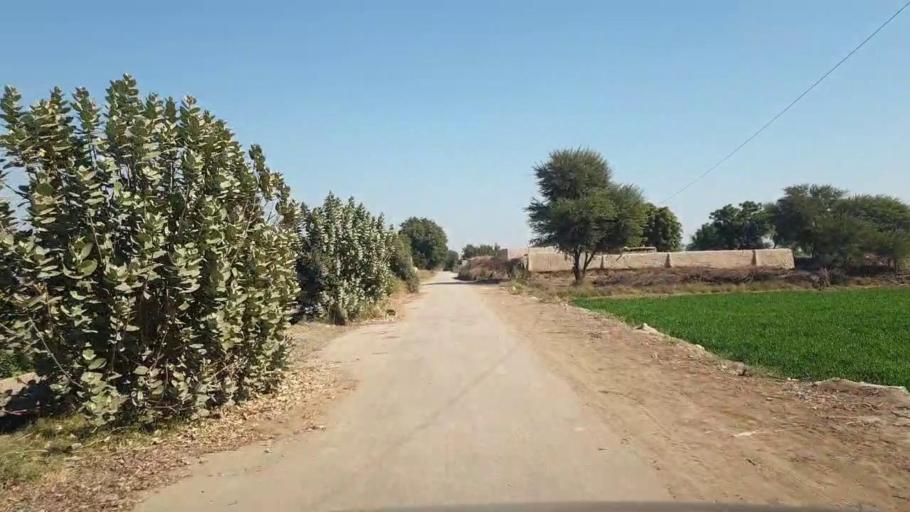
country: PK
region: Sindh
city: Shahpur Chakar
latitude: 26.1080
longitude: 68.6544
